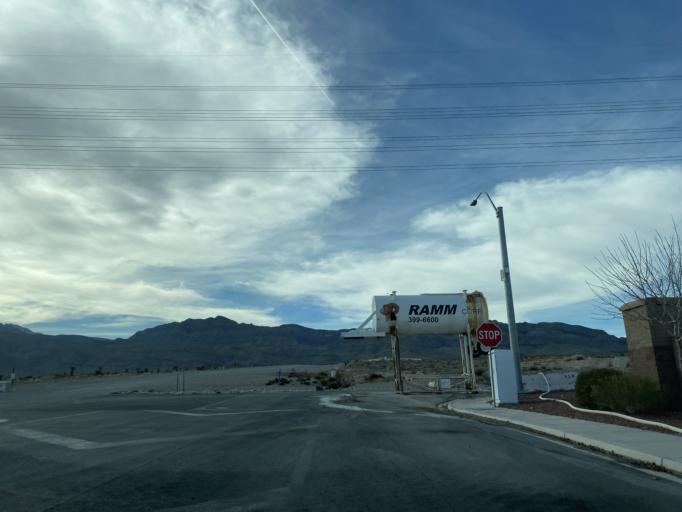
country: US
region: Nevada
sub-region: Clark County
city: Summerlin South
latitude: 36.2772
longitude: -115.3329
